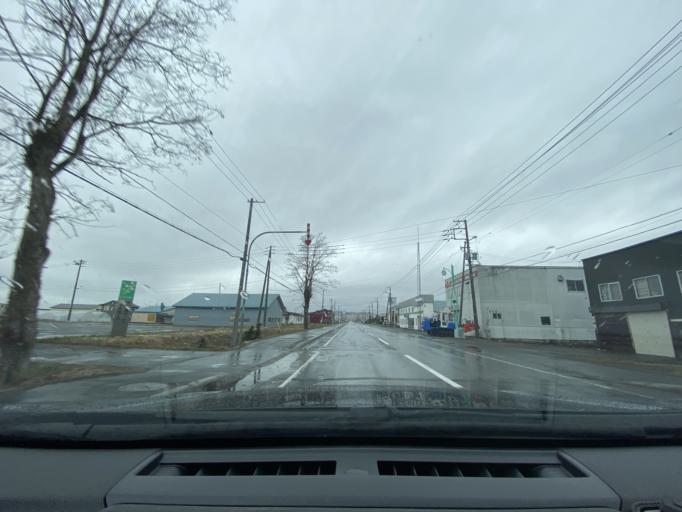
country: JP
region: Hokkaido
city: Fukagawa
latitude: 43.8076
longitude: 141.9233
